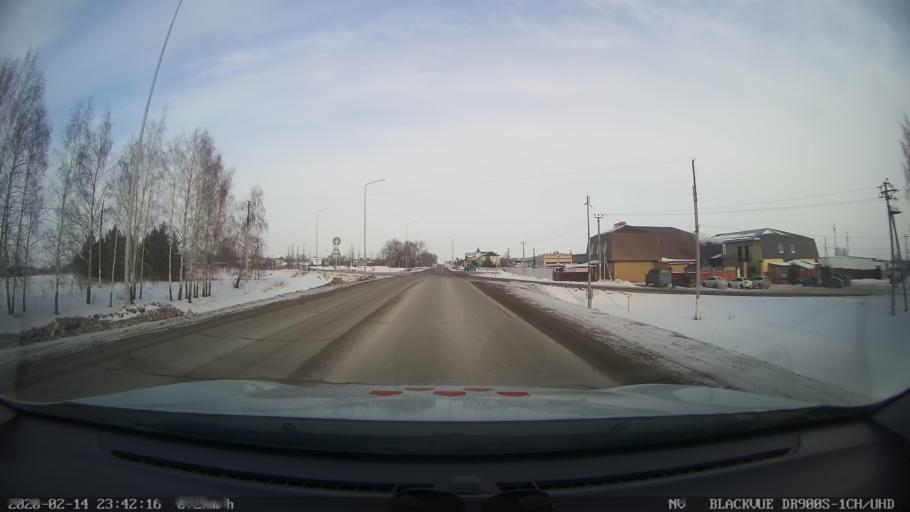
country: RU
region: Tatarstan
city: Kuybyshevskiy Zaton
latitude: 55.1905
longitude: 49.2468
